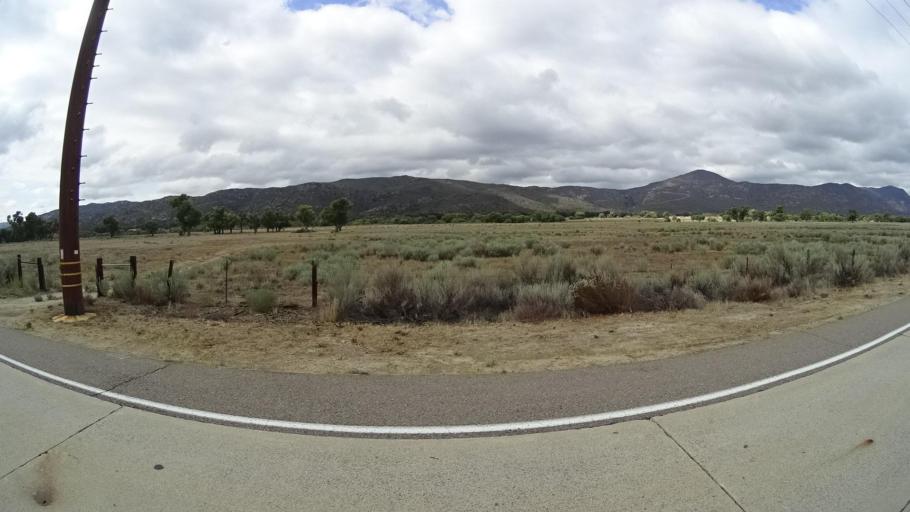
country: US
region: California
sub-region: San Diego County
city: Pine Valley
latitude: 32.7372
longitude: -116.4822
